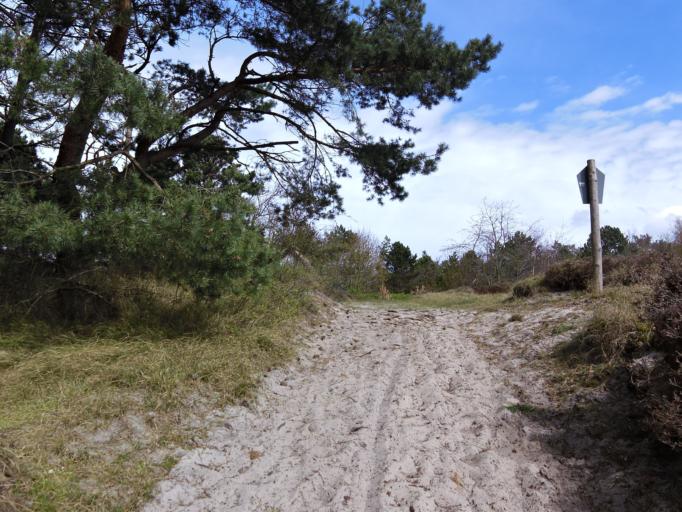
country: DE
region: Mecklenburg-Vorpommern
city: Hiddensee
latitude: 54.5452
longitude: 13.0938
